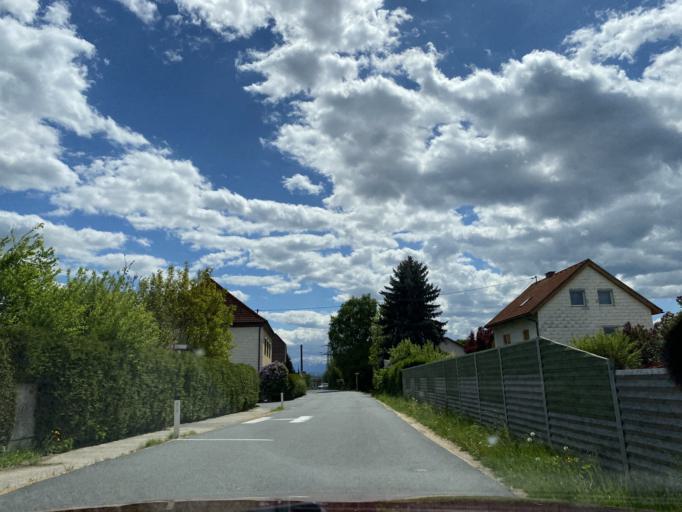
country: AT
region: Carinthia
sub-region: Politischer Bezirk Wolfsberg
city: Wolfsberg
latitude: 46.8504
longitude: 14.8404
